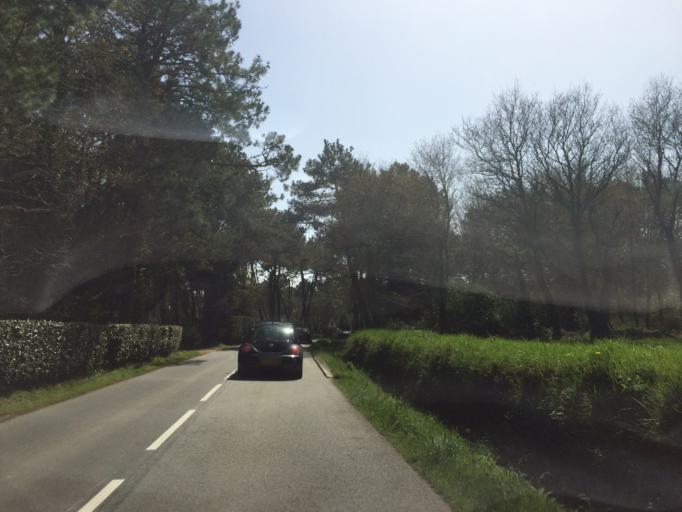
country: FR
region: Brittany
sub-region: Departement du Morbihan
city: Ploemel
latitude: 47.6289
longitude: -3.0495
